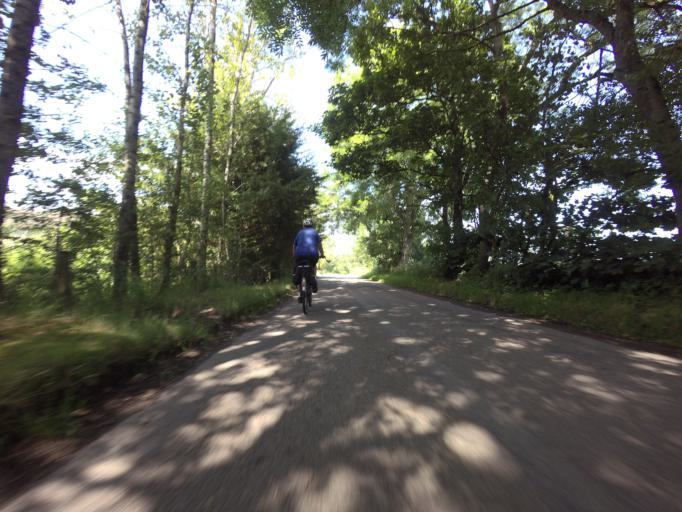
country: GB
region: Scotland
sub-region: Highland
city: Conon Bridge
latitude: 57.5548
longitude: -4.4080
